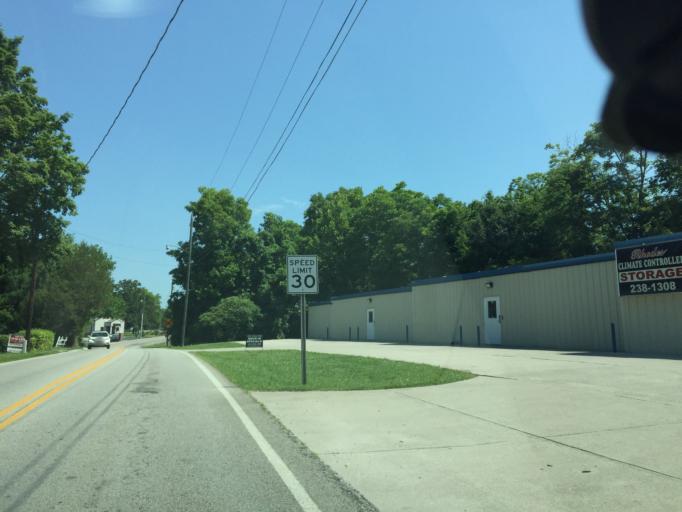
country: US
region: Tennessee
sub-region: Hamilton County
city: Collegedale
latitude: 35.0693
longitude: -85.0640
